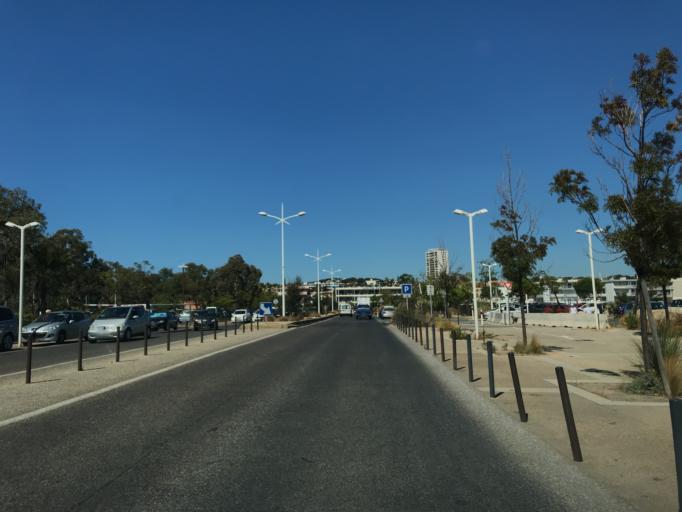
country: FR
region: Provence-Alpes-Cote d'Azur
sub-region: Departement du Var
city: La Seyne-sur-Mer
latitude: 43.0804
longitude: 5.8964
